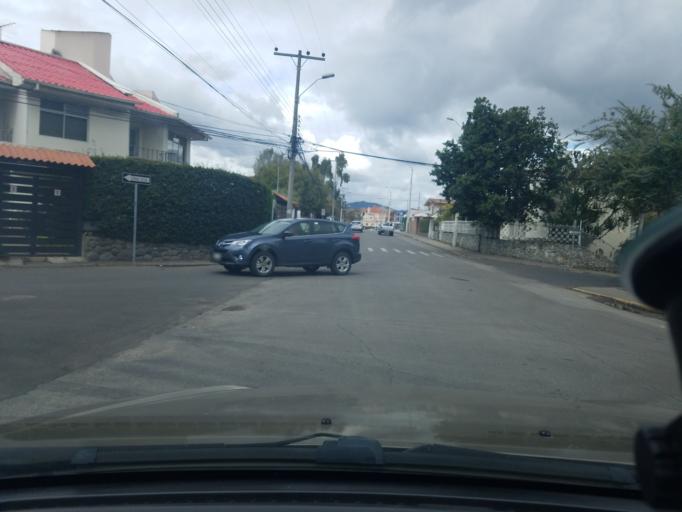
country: EC
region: Azuay
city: Cuenca
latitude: -2.9089
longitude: -79.0063
